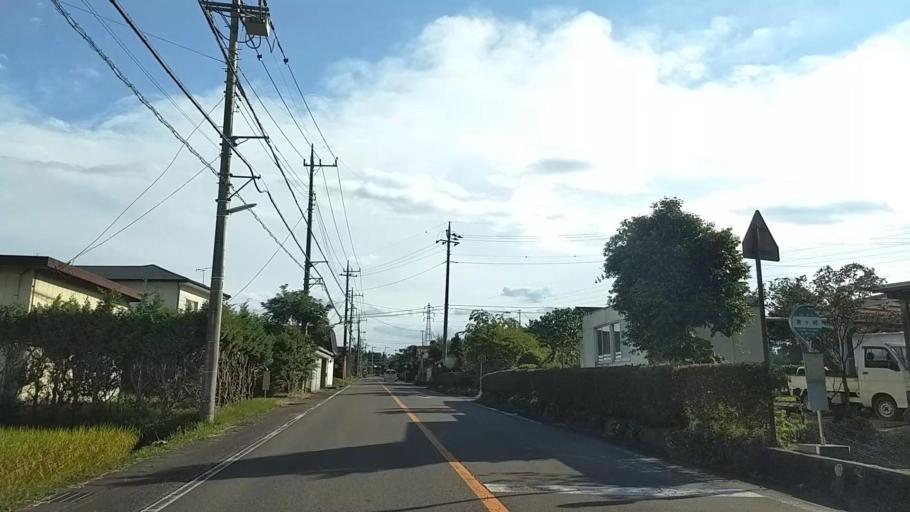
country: JP
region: Tochigi
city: Imaichi
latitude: 36.7472
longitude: 139.7074
